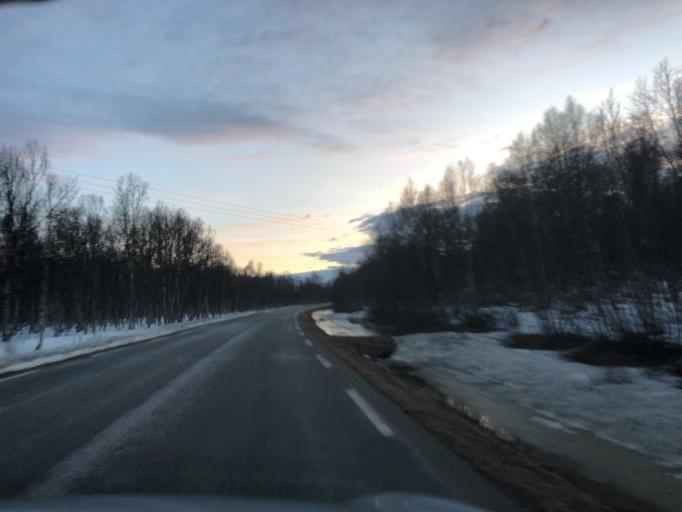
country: NO
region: Sor-Trondelag
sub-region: Tydal
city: Aas
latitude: 62.6723
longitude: 11.8264
